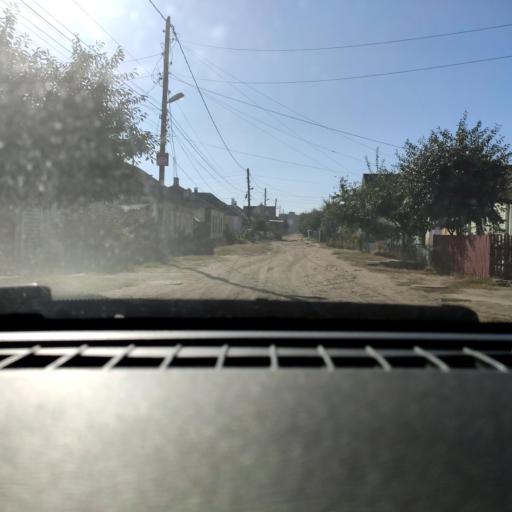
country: RU
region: Voronezj
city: Voronezh
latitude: 51.6672
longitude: 39.2867
